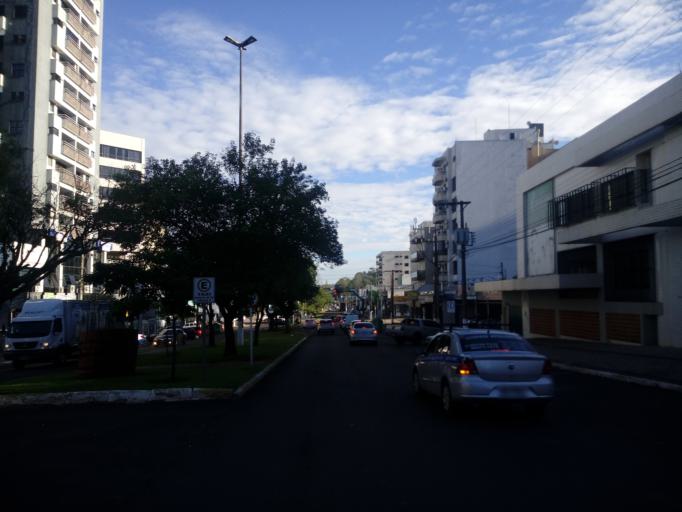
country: BR
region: Santa Catarina
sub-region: Chapeco
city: Chapeco
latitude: -27.0930
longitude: -52.6175
